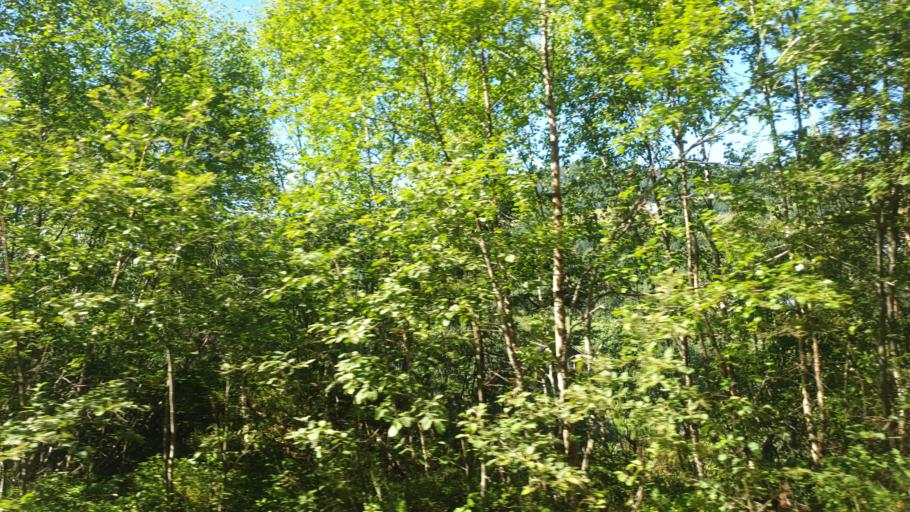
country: NO
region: Sor-Trondelag
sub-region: Meldal
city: Meldal
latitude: 63.1721
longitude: 9.7486
